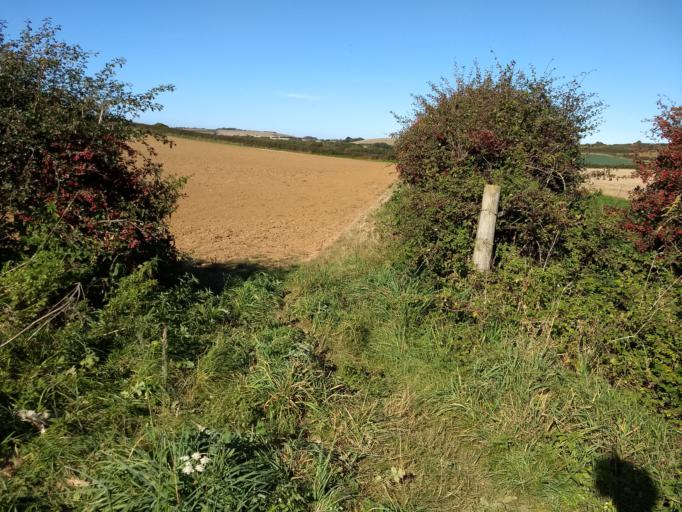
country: GB
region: England
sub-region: Isle of Wight
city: Niton
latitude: 50.6320
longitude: -1.2858
